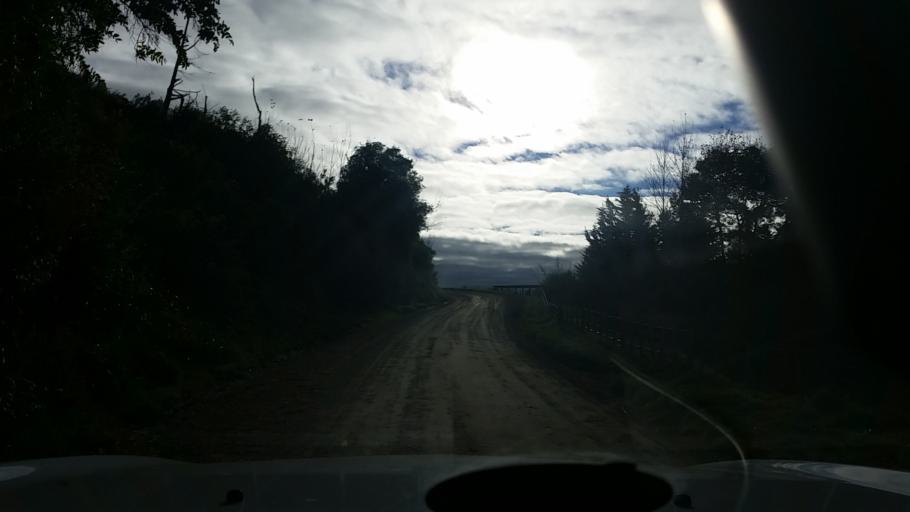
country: NZ
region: Hawke's Bay
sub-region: Napier City
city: Napier
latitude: -39.2632
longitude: 176.8512
